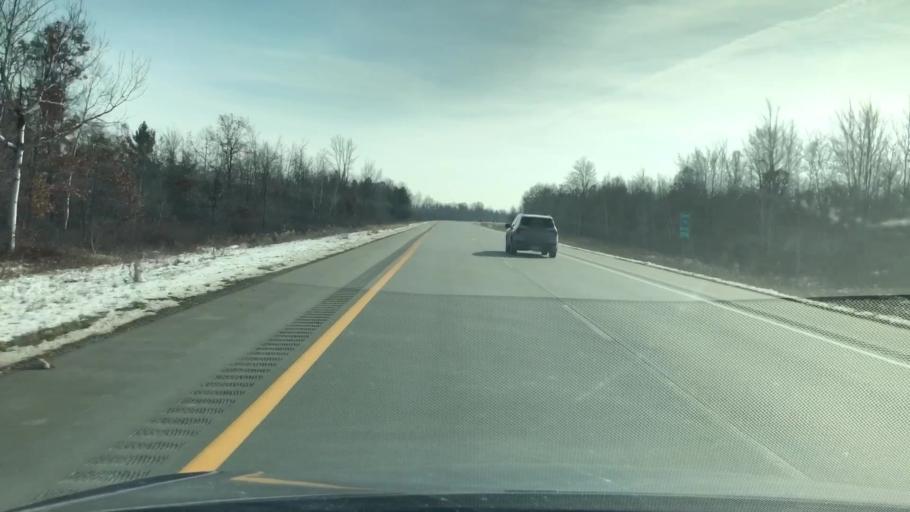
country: US
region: Michigan
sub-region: Ogemaw County
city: Skidway Lake
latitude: 44.0995
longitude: -84.1148
